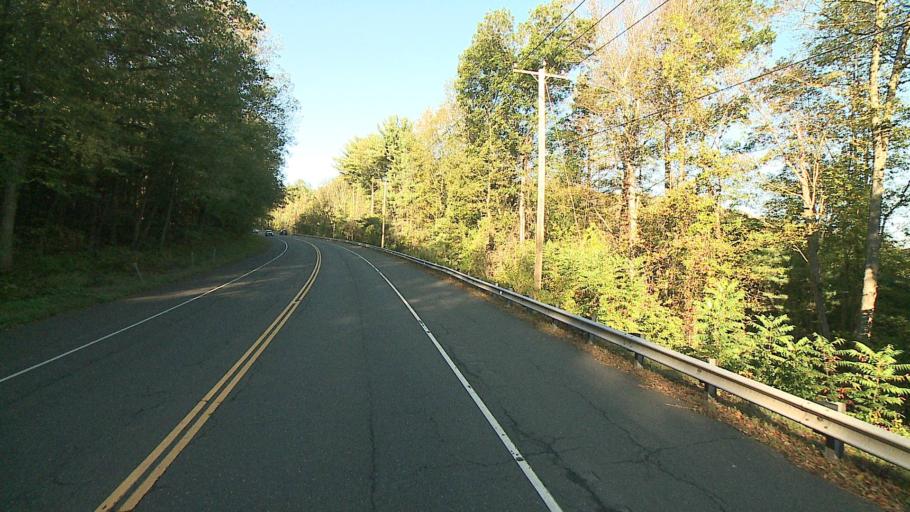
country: US
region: Connecticut
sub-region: Hartford County
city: Collinsville
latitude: 41.8335
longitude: -72.9350
